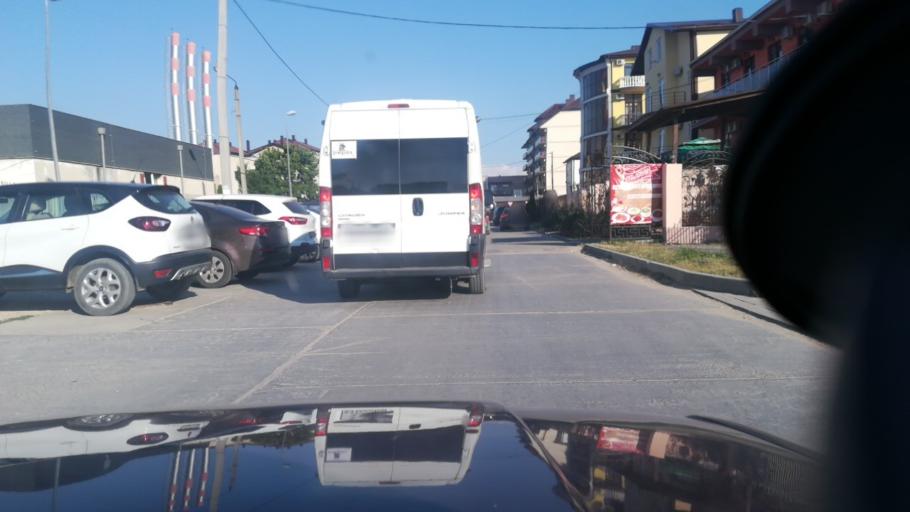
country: RU
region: Krasnodarskiy
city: Vityazevo
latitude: 44.9879
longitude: 37.2498
